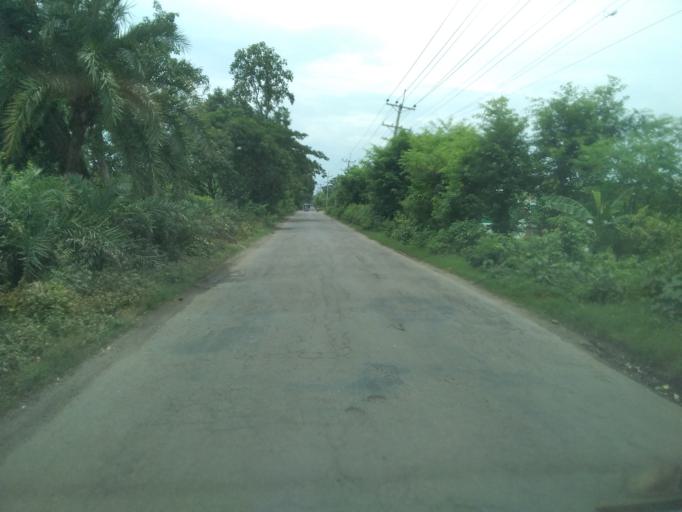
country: IN
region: West Bengal
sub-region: North 24 Parganas
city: Taki
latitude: 22.5693
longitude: 89.0015
